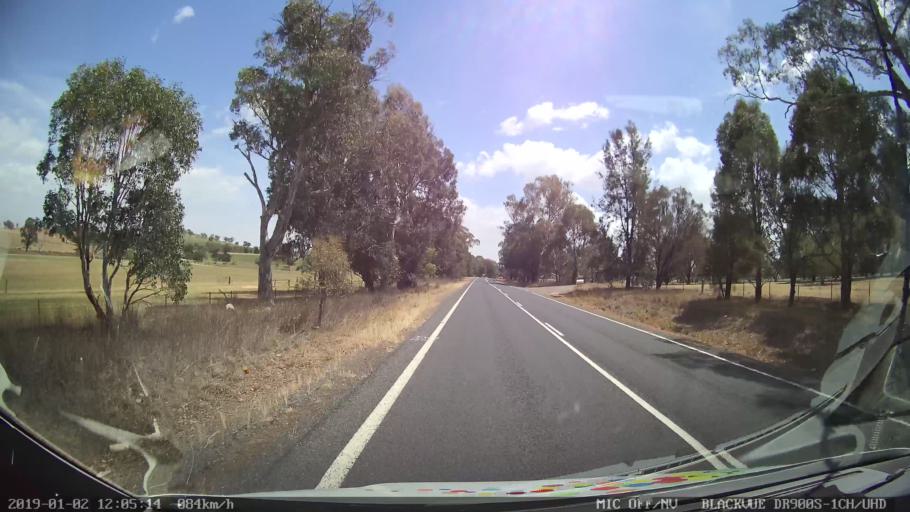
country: AU
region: New South Wales
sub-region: Young
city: Young
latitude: -34.5167
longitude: 148.3030
